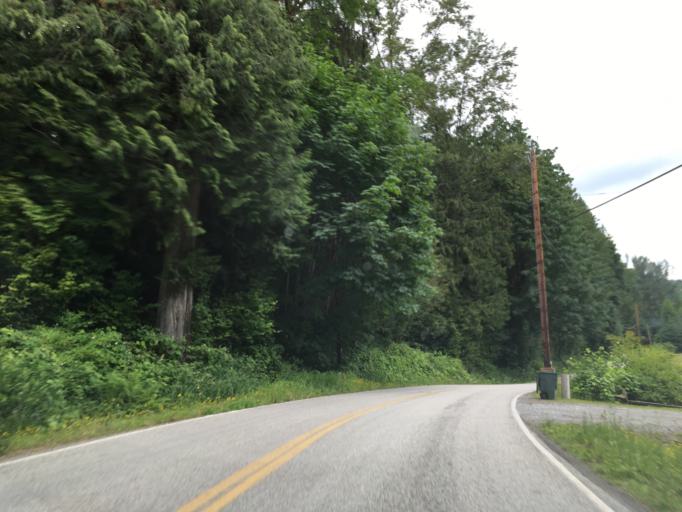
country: US
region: Washington
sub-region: Whatcom County
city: Peaceful Valley
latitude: 48.9423
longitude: -122.0765
